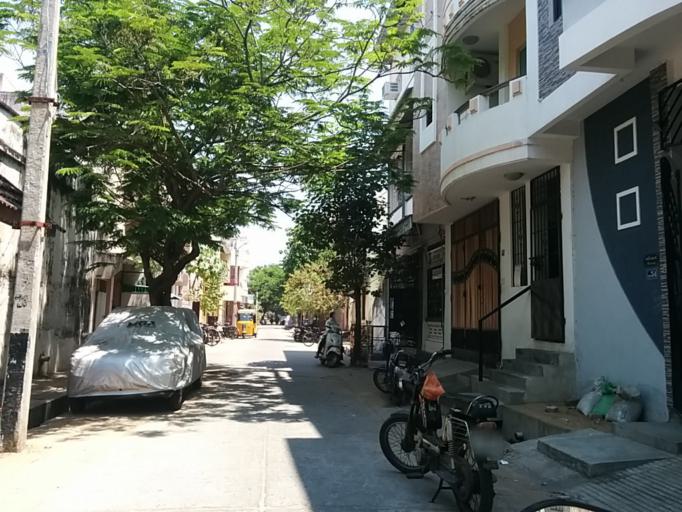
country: IN
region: Pondicherry
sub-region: Puducherry
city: Puducherry
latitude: 11.9260
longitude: 79.8299
